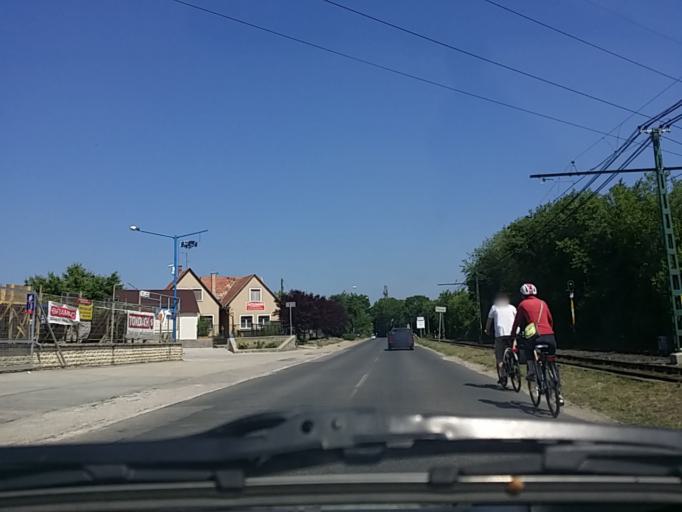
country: HU
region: Pest
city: Pomaz
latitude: 47.6376
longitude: 19.0388
